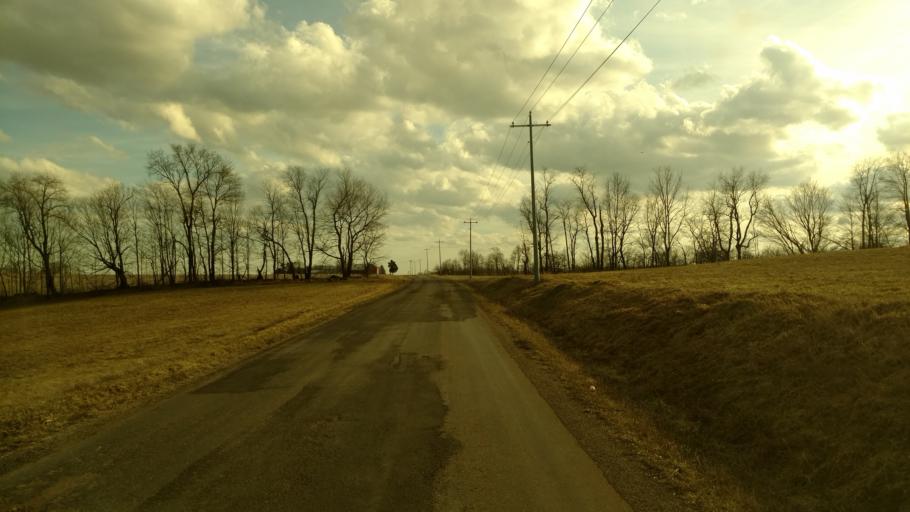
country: US
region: Ohio
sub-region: Sandusky County
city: Bellville
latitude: 40.5445
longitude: -82.4498
